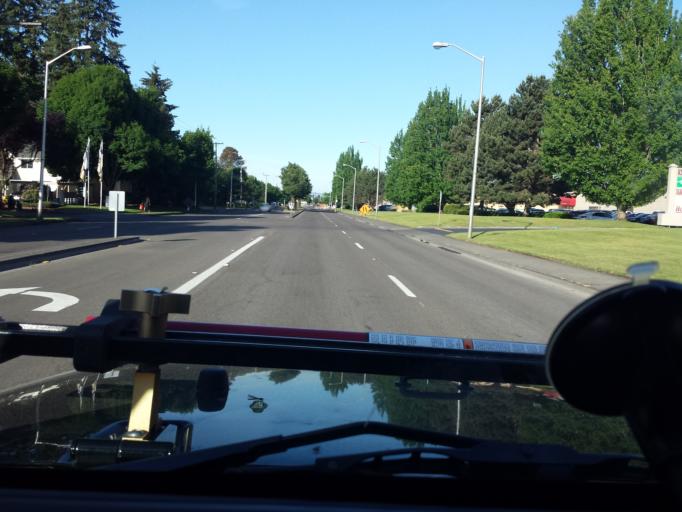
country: US
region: Washington
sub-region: Clark County
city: Walnut Grove
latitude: 45.6483
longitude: -122.5901
